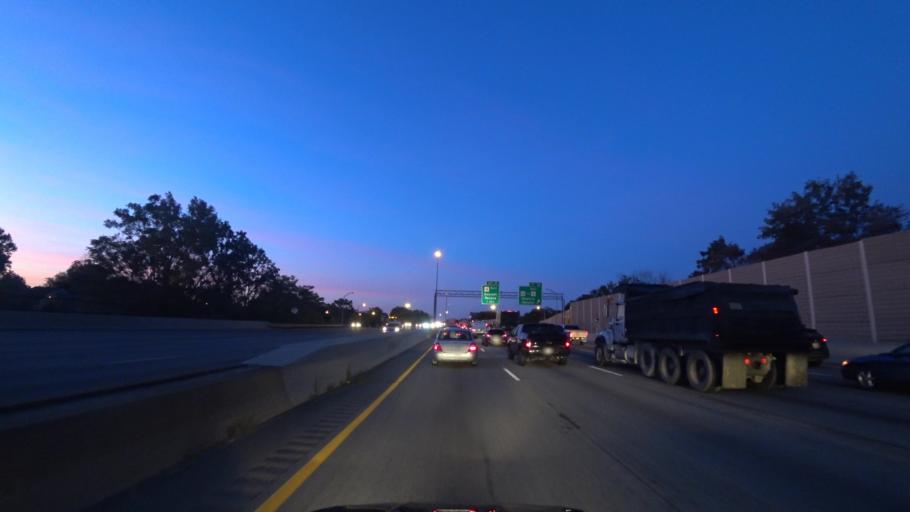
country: US
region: Massachusetts
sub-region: Middlesex County
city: Medford
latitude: 42.4233
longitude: -71.1036
